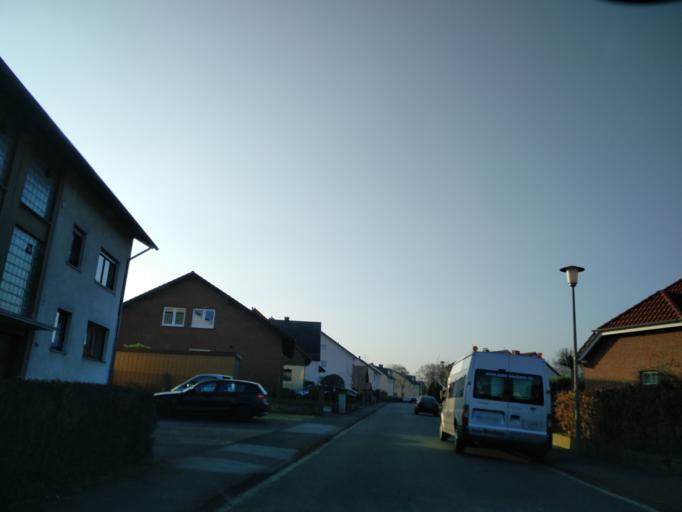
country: DE
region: North Rhine-Westphalia
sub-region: Regierungsbezirk Detmold
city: Paderborn
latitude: 51.6895
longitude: 8.6910
